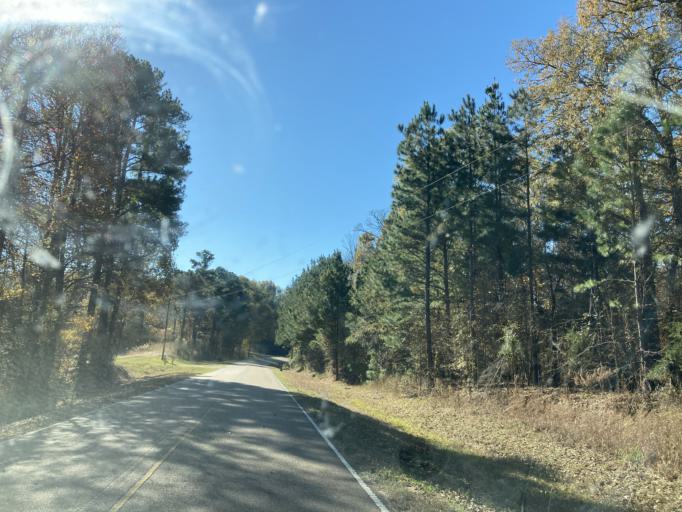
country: US
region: Mississippi
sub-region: Hinds County
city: Lynchburg
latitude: 32.6210
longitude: -90.5241
